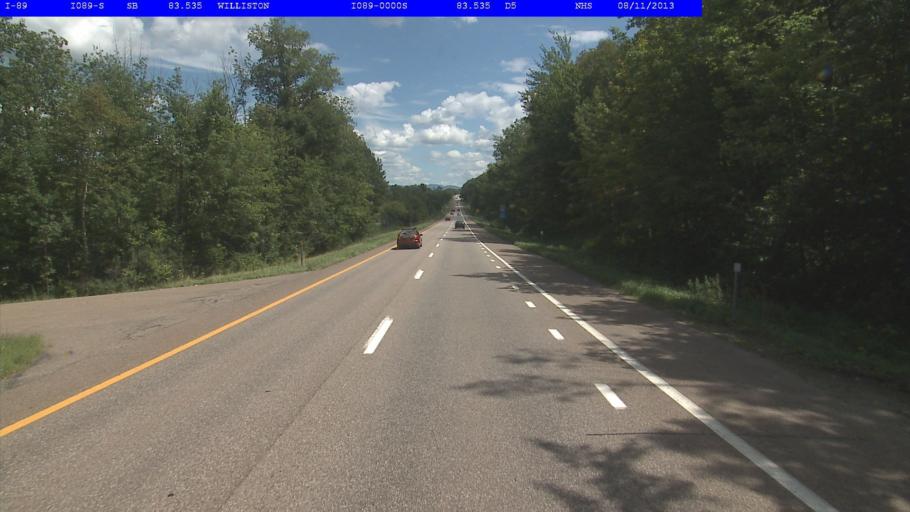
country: US
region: Vermont
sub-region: Chittenden County
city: Williston
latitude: 44.4383
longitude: -73.1067
